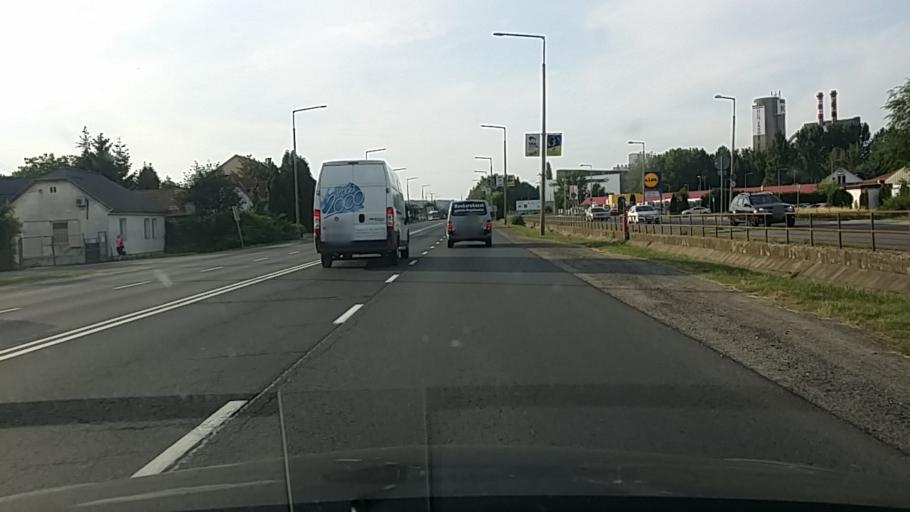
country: HU
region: Borsod-Abauj-Zemplen
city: Miskolc
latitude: 48.0585
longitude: 20.7965
